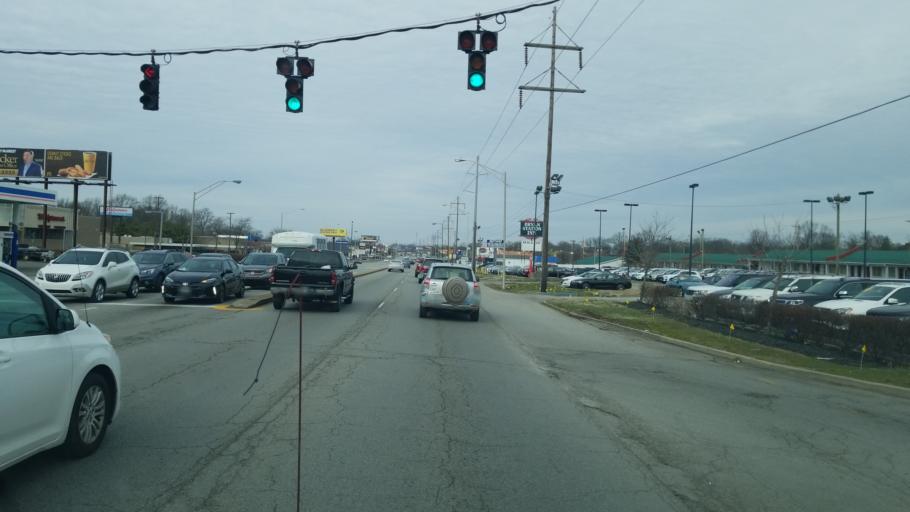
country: US
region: Kentucky
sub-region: Fayette County
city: Lexington-Fayette
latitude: 38.0601
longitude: -84.4648
